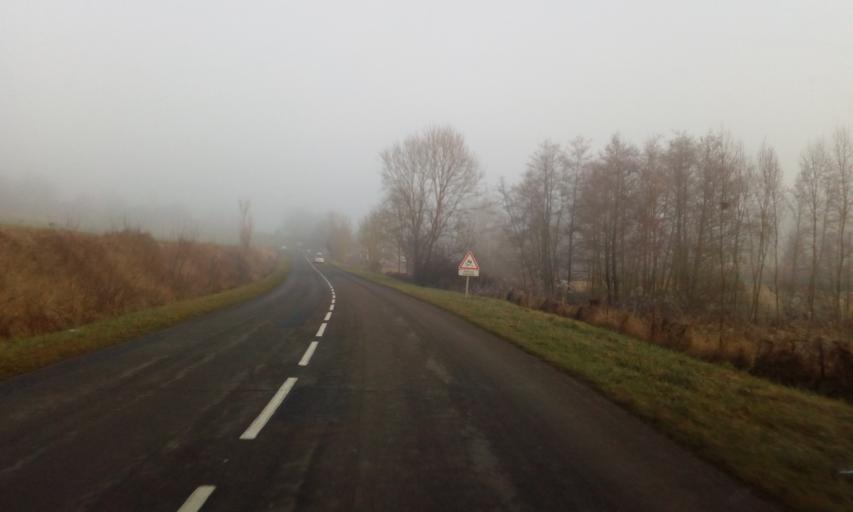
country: FR
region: Champagne-Ardenne
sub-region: Departement des Ardennes
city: Rimogne
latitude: 49.7758
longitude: 4.4475
